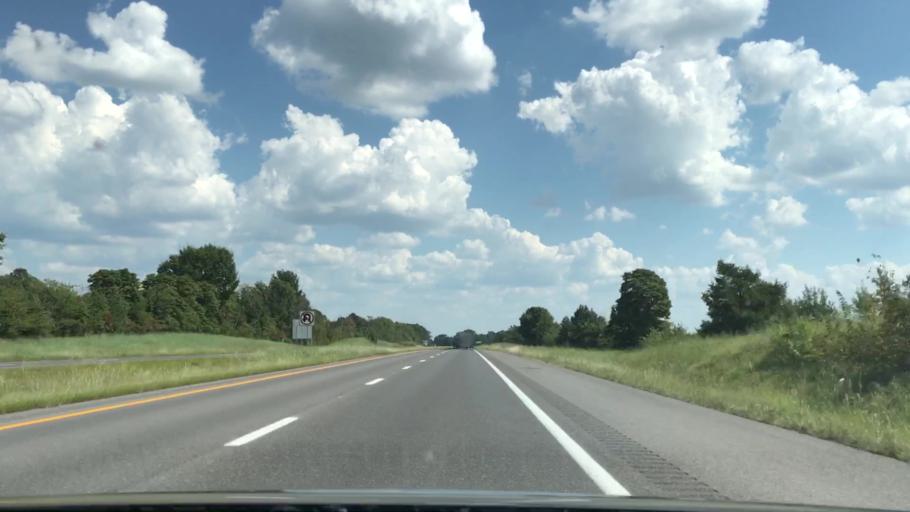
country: US
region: Kentucky
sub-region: Lyon County
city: Eddyville
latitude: 37.1079
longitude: -87.9978
